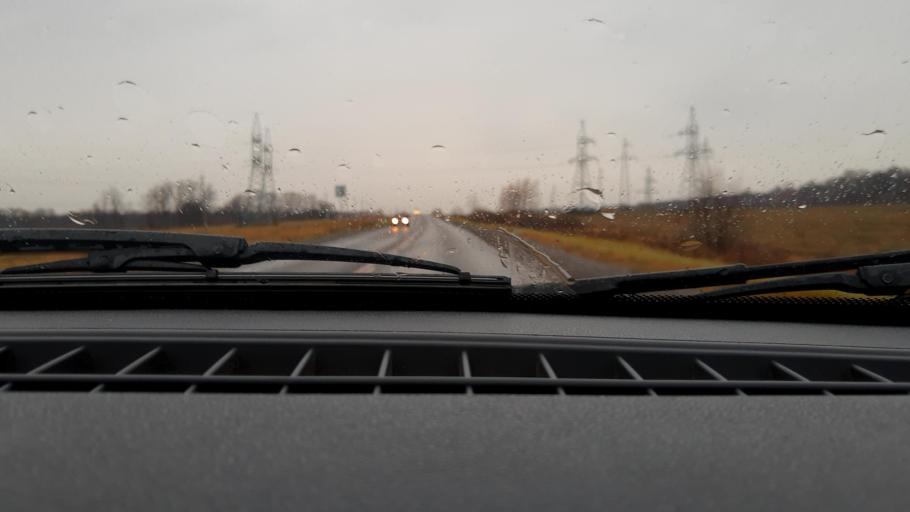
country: RU
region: Bashkortostan
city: Mikhaylovka
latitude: 54.8327
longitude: 55.9261
